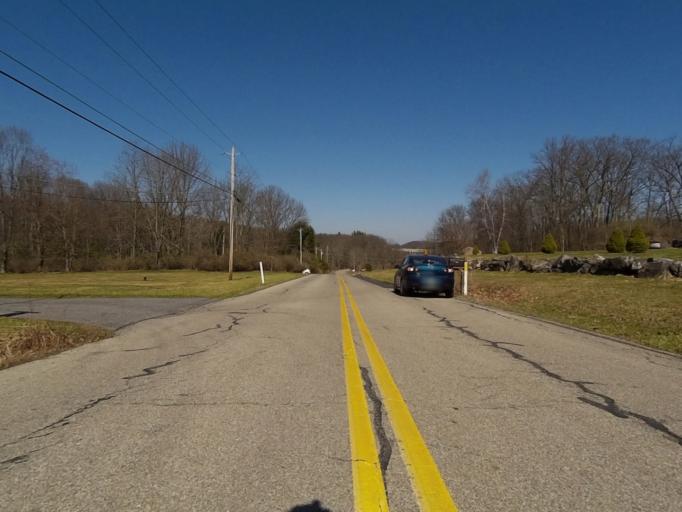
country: US
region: Pennsylvania
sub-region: Centre County
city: Park Forest Village
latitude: 40.8172
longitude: -77.9547
